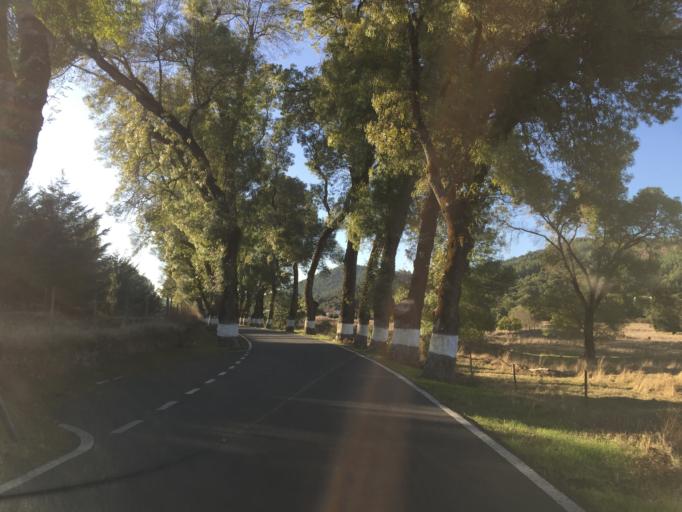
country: PT
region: Portalegre
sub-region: Marvao
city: Marvao
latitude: 39.3830
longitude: -7.3945
